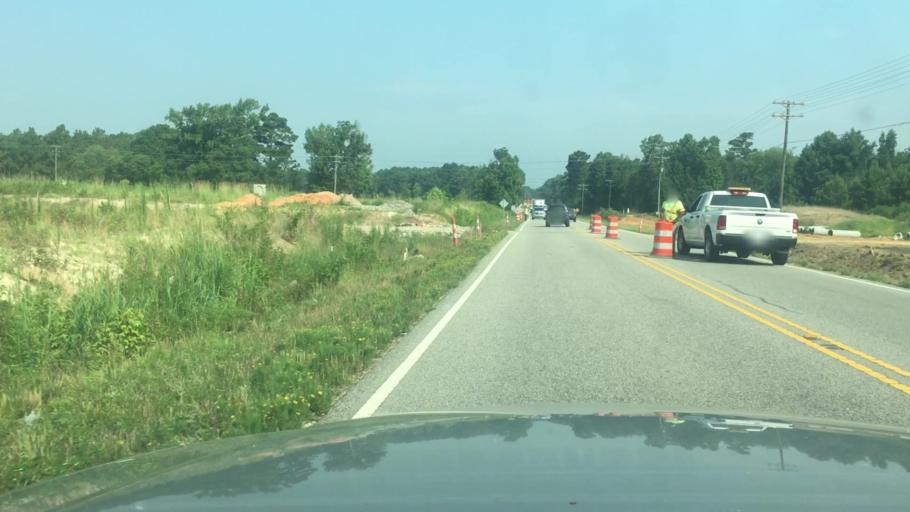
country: US
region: North Carolina
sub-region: Cumberland County
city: Hope Mills
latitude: 34.9273
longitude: -78.9115
